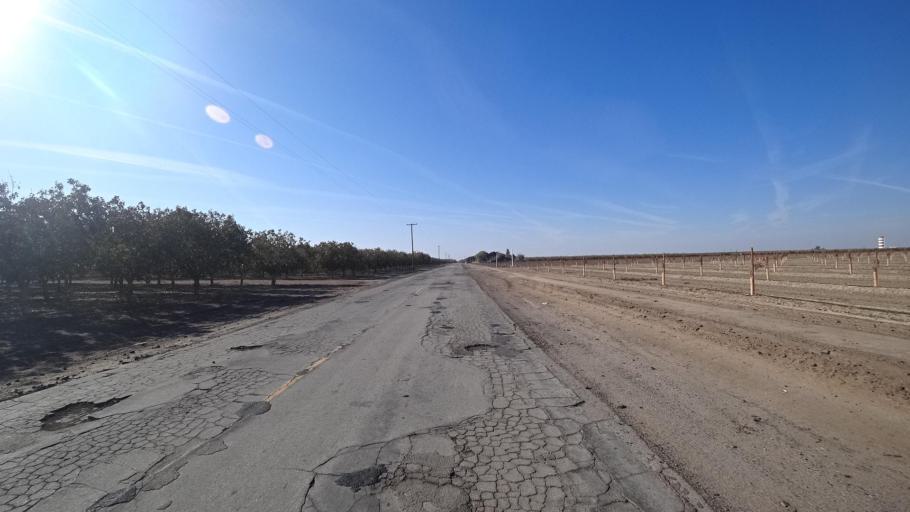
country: US
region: California
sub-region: Kern County
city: Wasco
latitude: 35.6524
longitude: -119.3434
